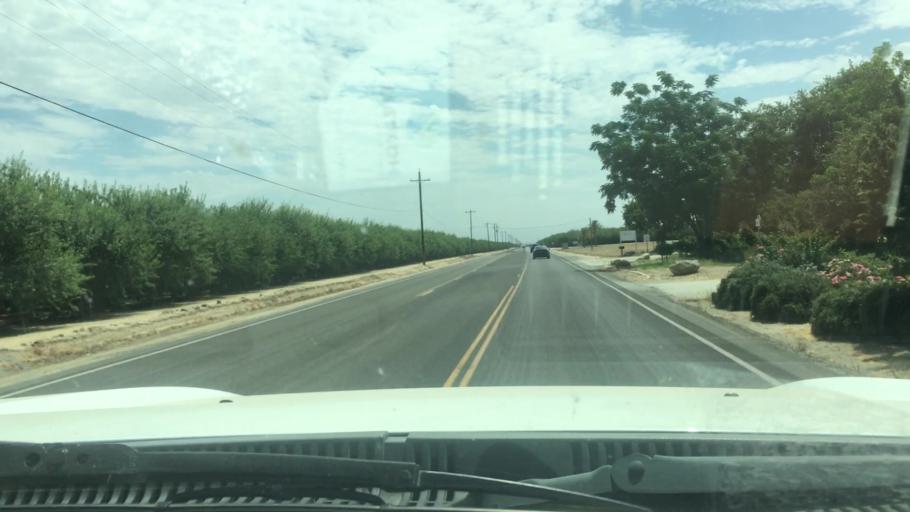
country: US
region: California
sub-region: Kern County
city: Wasco
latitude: 35.5580
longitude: -119.3261
